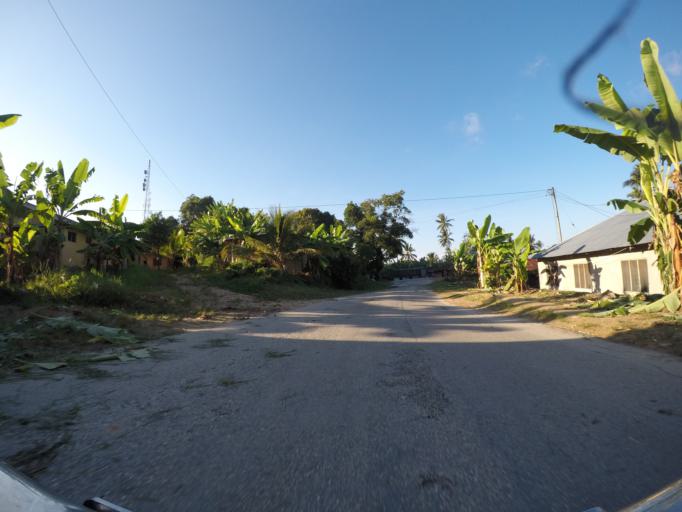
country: TZ
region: Pemba South
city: Mtambile
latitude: -5.3795
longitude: 39.6942
